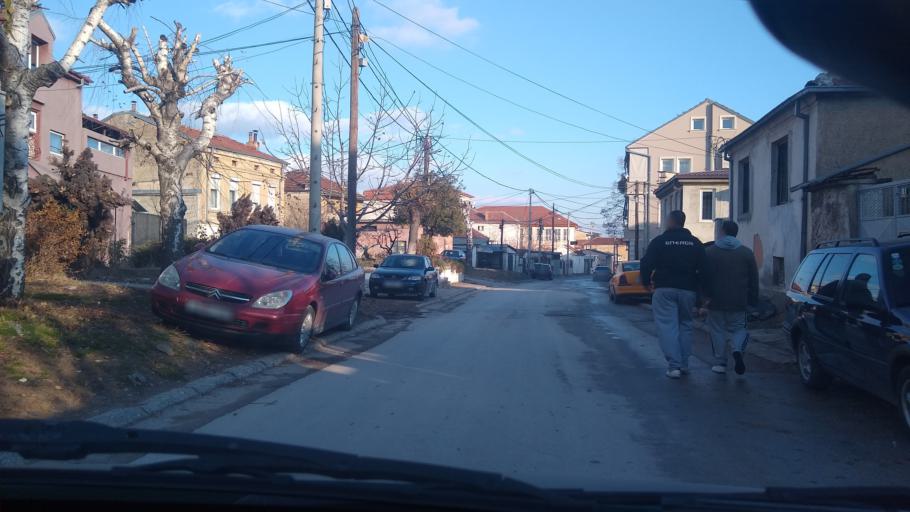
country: MK
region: Bitola
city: Bitola
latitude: 41.0309
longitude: 21.3251
